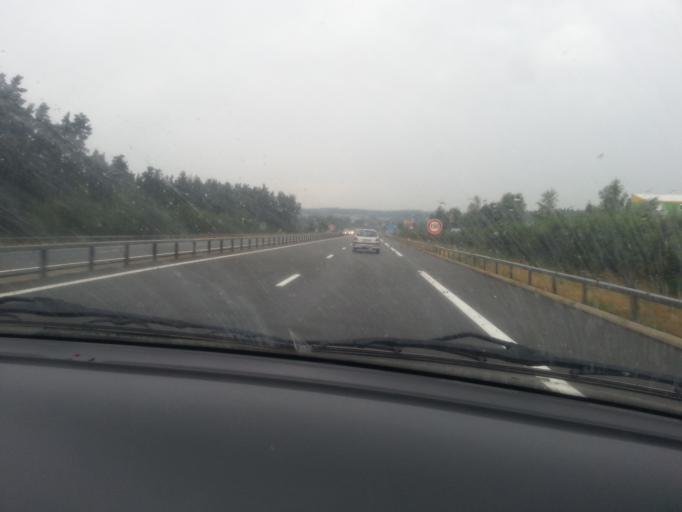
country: FR
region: Languedoc-Roussillon
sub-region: Departement de la Lozere
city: Aumont-Aubrac
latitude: 44.7379
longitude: 3.2892
